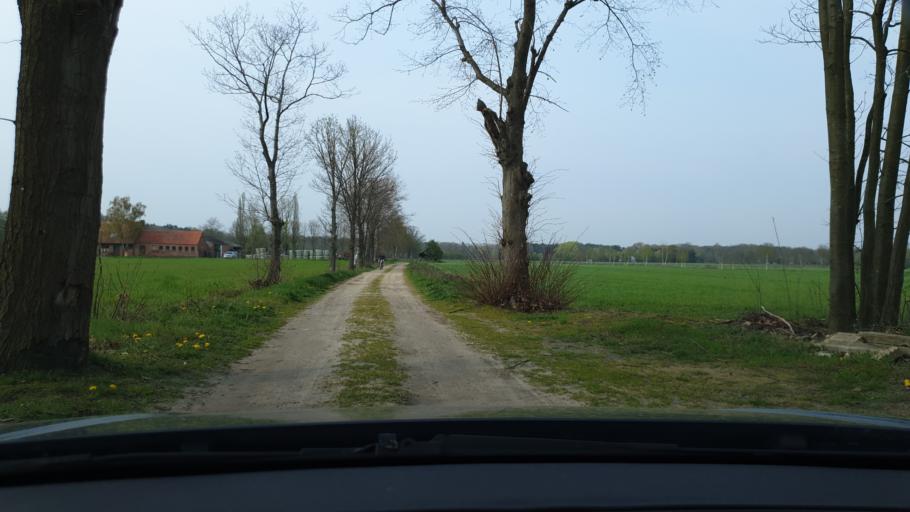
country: BE
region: Flanders
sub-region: Provincie Antwerpen
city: Laakdal
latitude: 51.1257
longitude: 5.0222
